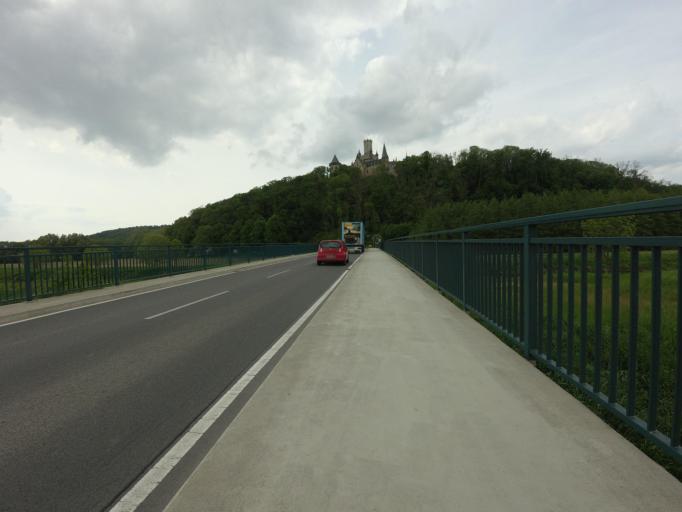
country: DE
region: Lower Saxony
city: Nordstemmen
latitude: 52.1704
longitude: 9.7696
